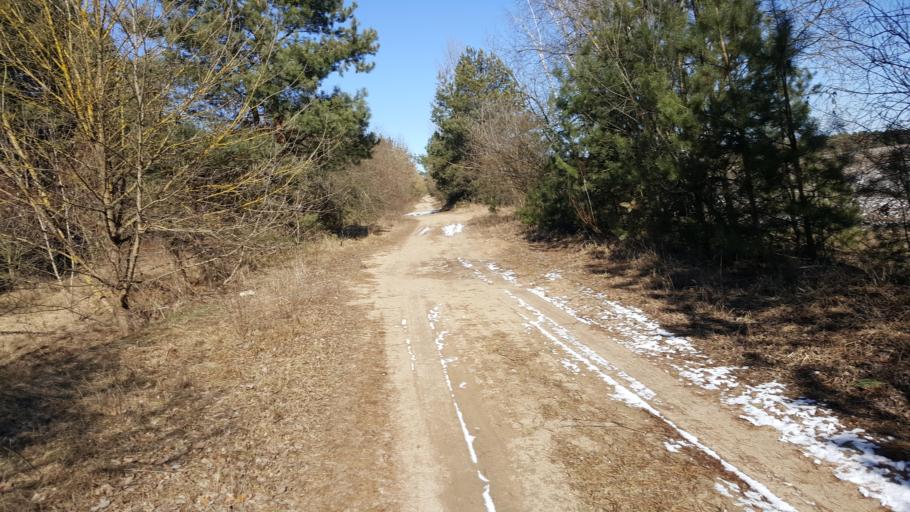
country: BY
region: Brest
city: Kamyanyets
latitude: 52.3823
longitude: 23.8428
